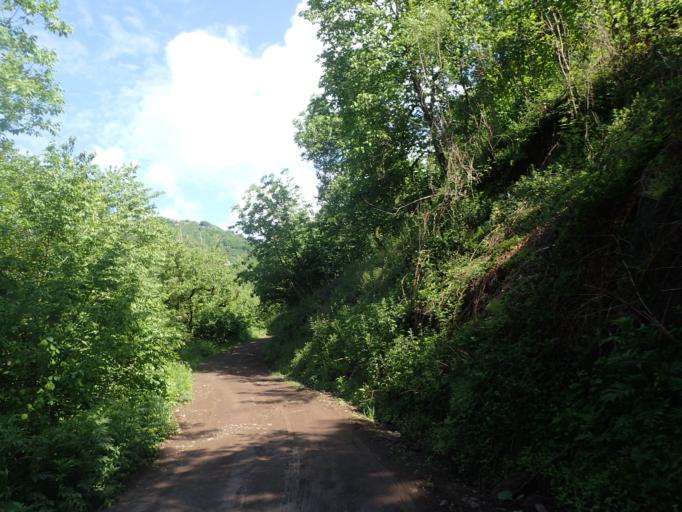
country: TR
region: Samsun
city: Salipazari
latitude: 40.9214
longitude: 36.8500
